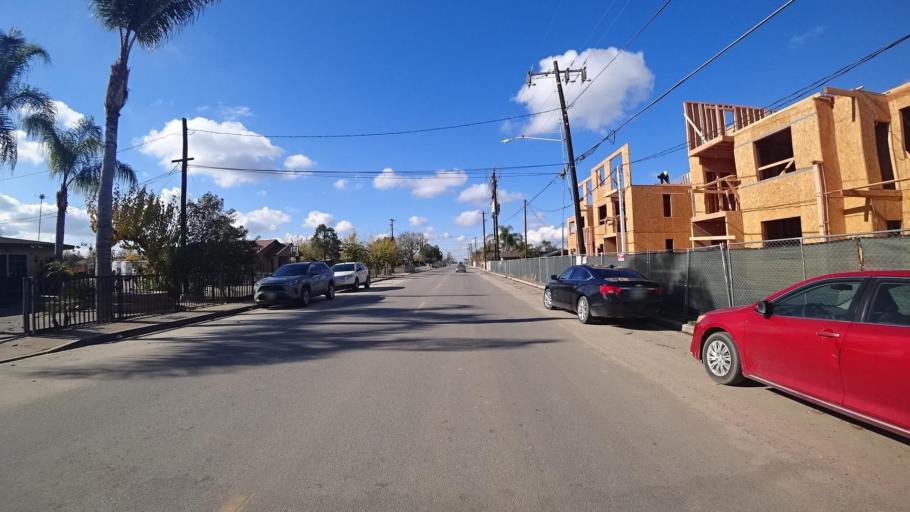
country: US
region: California
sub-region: Kern County
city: McFarland
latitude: 35.6744
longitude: -119.2377
